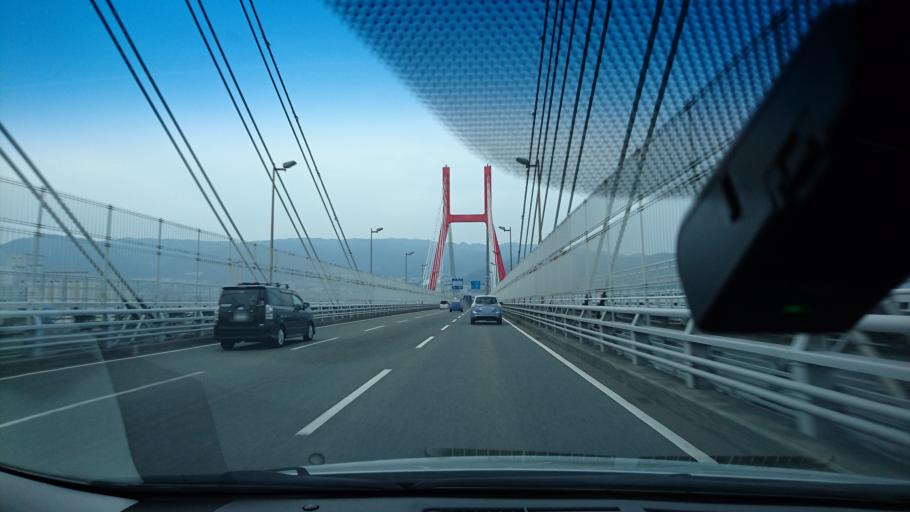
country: JP
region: Hyogo
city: Ashiya
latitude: 34.6992
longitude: 135.2678
